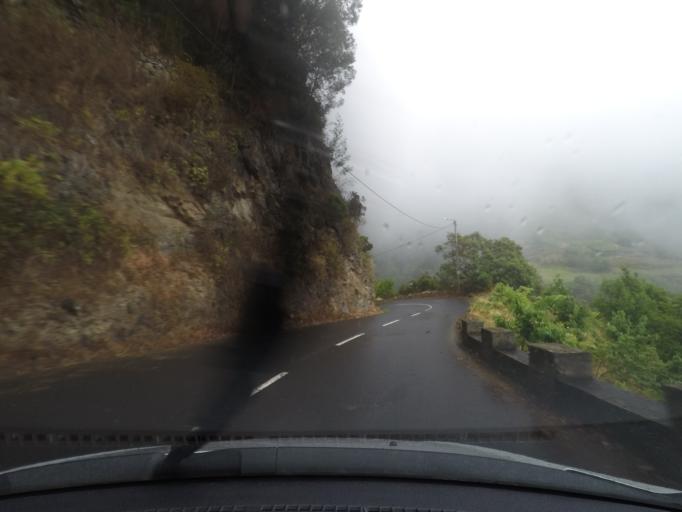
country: PT
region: Madeira
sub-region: Santana
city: Santana
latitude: 32.7745
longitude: -16.8735
